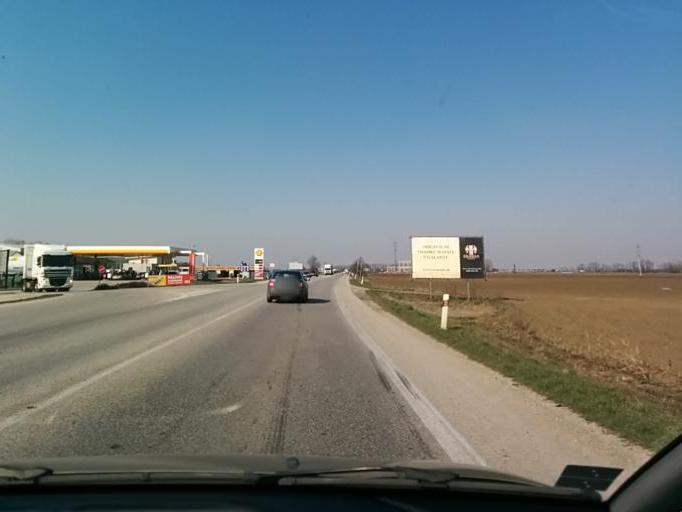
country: SK
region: Trnavsky
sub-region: Okres Galanta
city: Galanta
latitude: 48.2024
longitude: 17.7311
